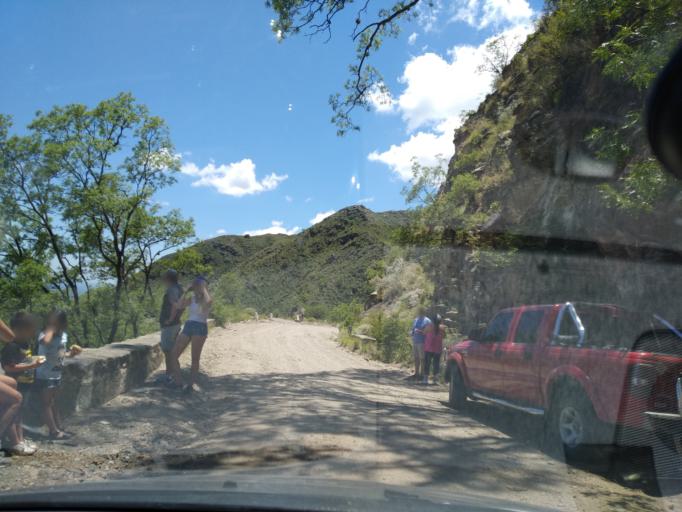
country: AR
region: Cordoba
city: Salsacate
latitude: -31.3751
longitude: -65.4076
